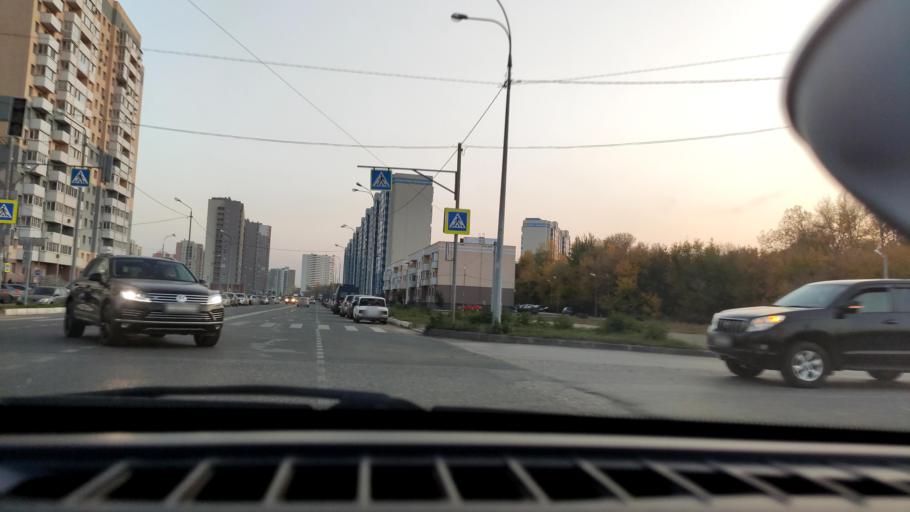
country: RU
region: Samara
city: Rozhdestveno
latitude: 53.1562
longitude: 50.0755
